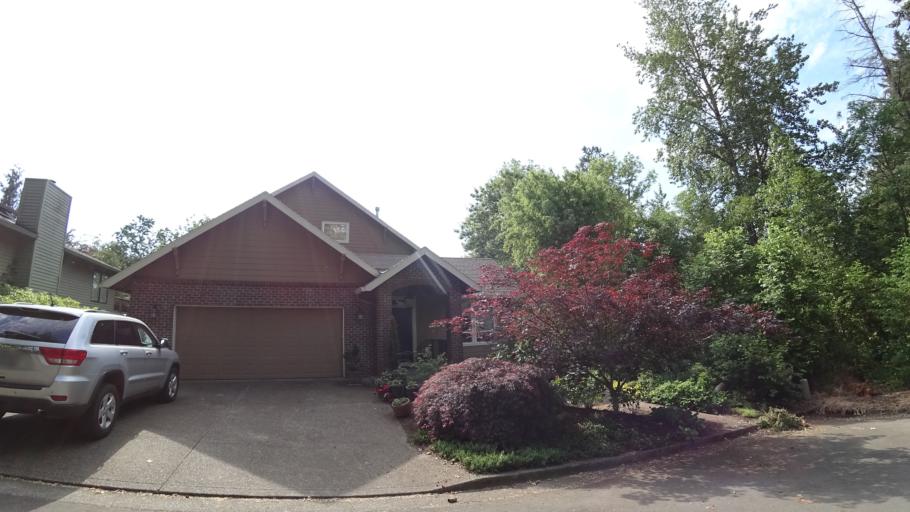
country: US
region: Oregon
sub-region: Washington County
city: Garden Home-Whitford
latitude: 45.4599
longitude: -122.7489
